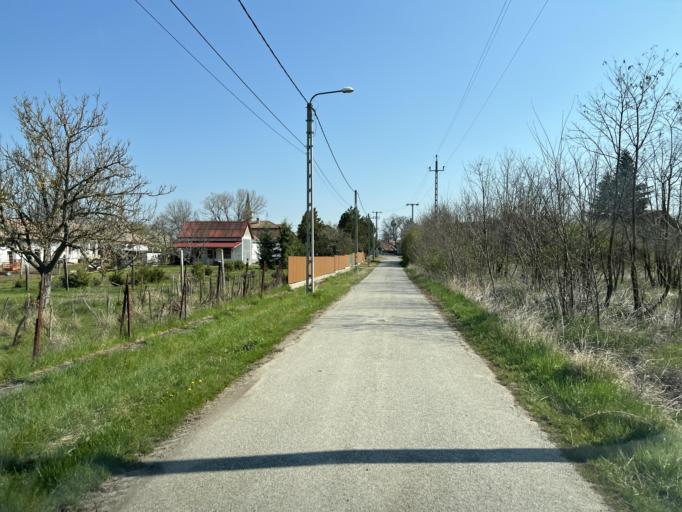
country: SK
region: Nitriansky
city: Zeliezovce
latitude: 47.9754
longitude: 18.7819
